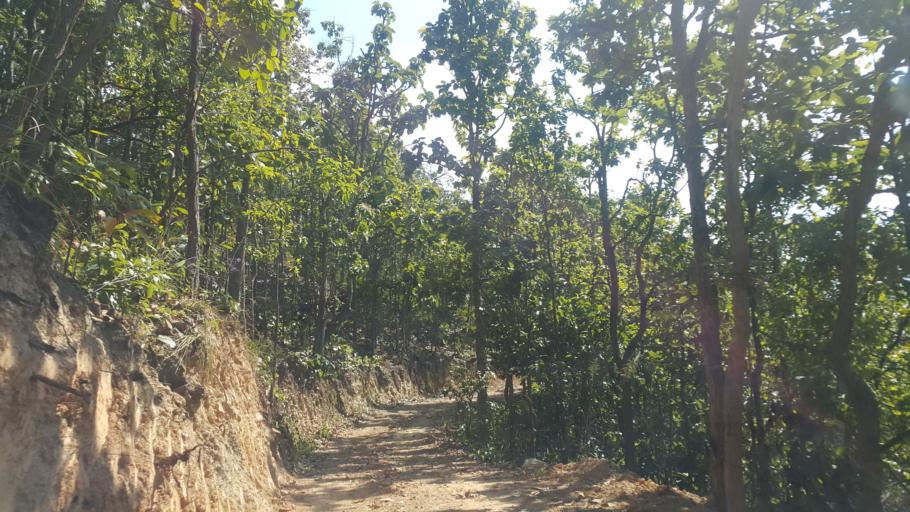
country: TH
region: Lamphun
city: Ban Thi
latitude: 18.6635
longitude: 99.1977
